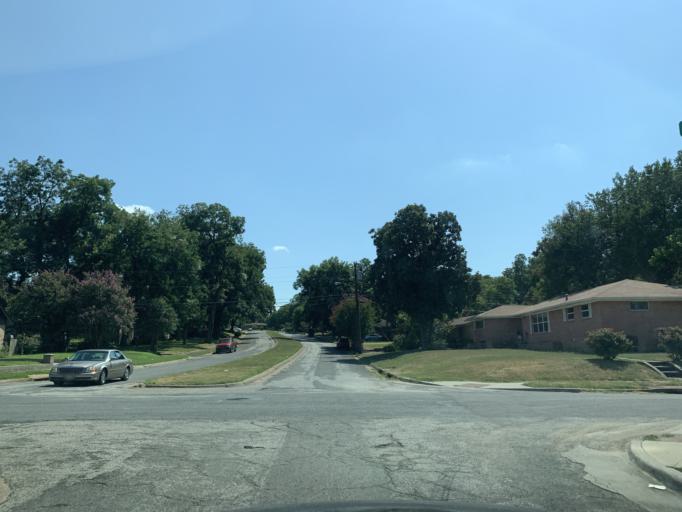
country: US
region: Texas
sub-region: Dallas County
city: Hutchins
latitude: 32.6789
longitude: -96.7963
